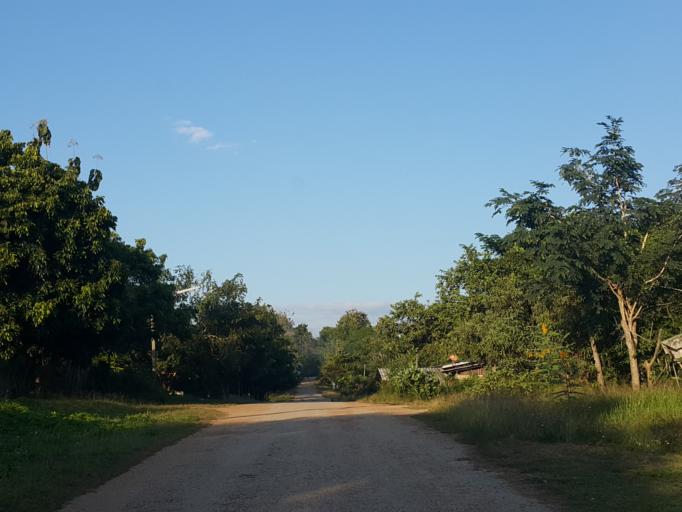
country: TH
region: Lampang
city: Lampang
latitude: 18.4213
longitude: 99.5542
